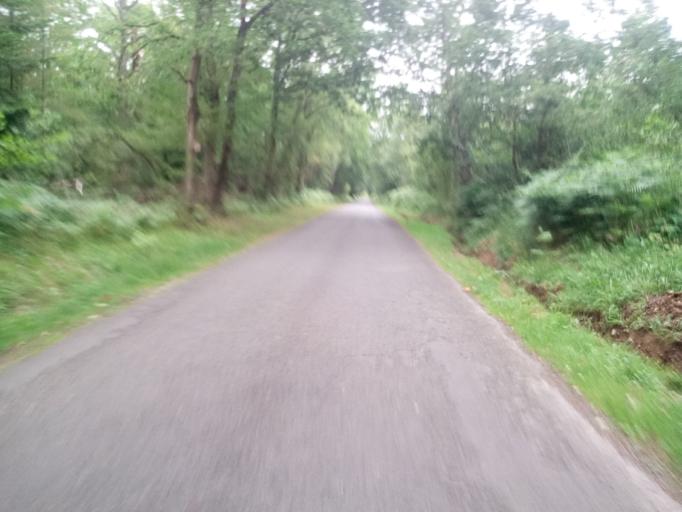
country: FR
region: Lower Normandy
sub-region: Departement du Calvados
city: Clinchamps-sur-Orne
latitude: 49.0275
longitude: -0.3956
